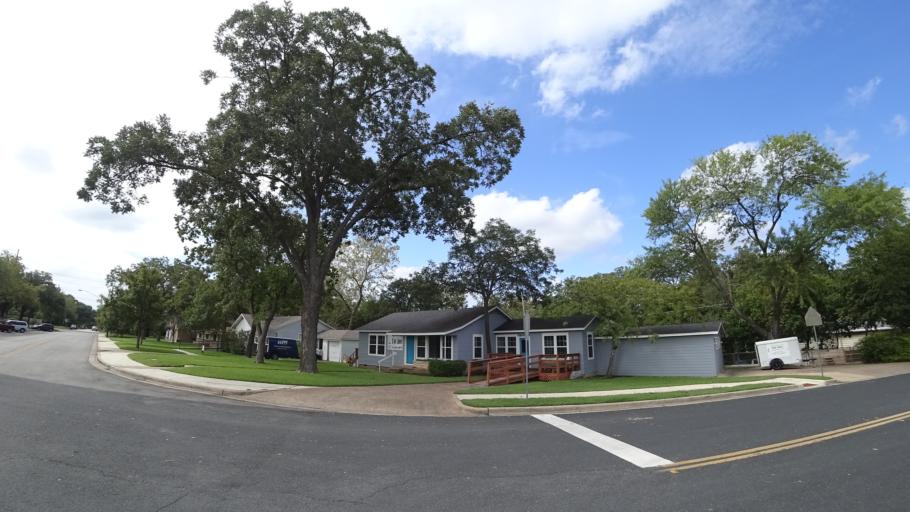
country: US
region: Texas
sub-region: Travis County
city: Austin
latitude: 30.3364
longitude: -97.7417
